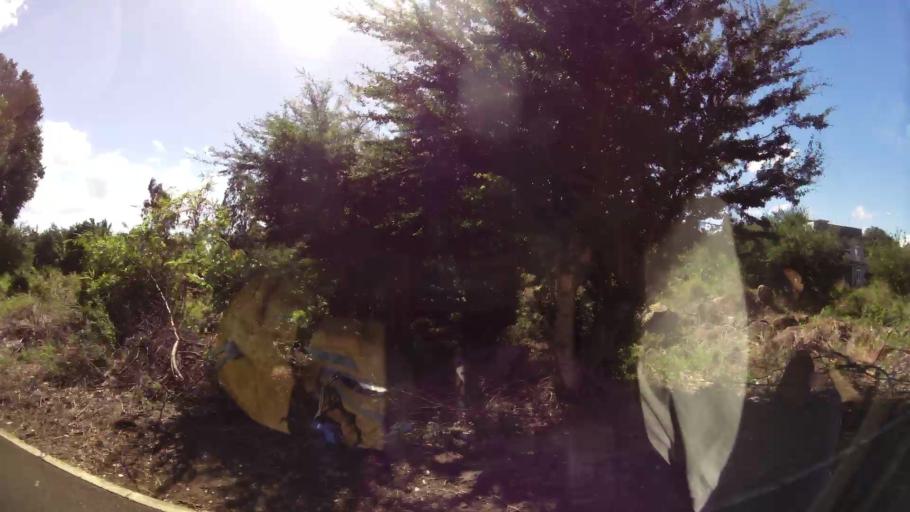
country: MU
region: Black River
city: Cascavelle
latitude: -20.2635
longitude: 57.4110
